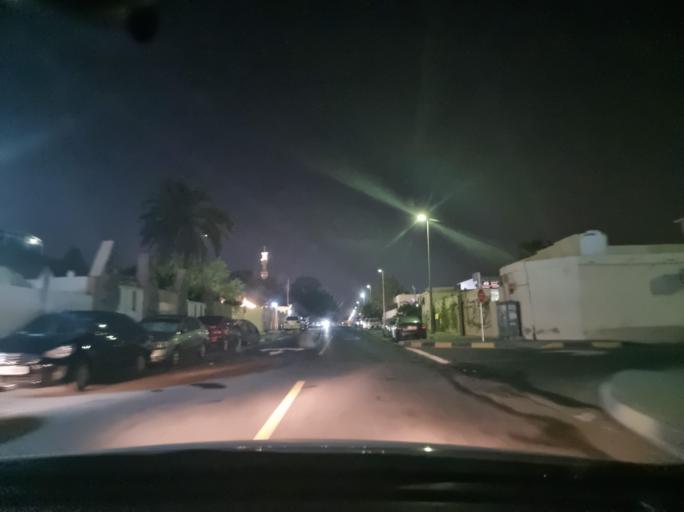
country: AE
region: Ash Shariqah
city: Sharjah
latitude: 25.3712
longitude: 55.4235
